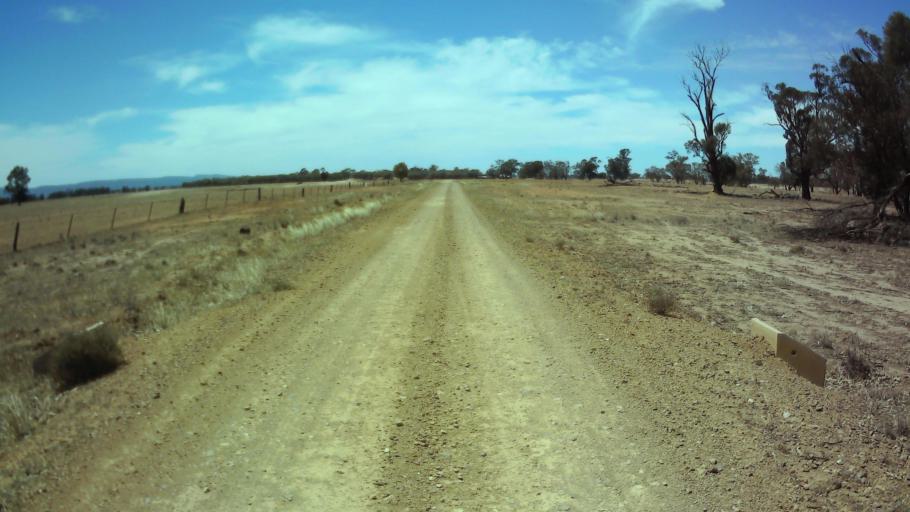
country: AU
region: New South Wales
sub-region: Weddin
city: Grenfell
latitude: -33.8635
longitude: 147.7601
